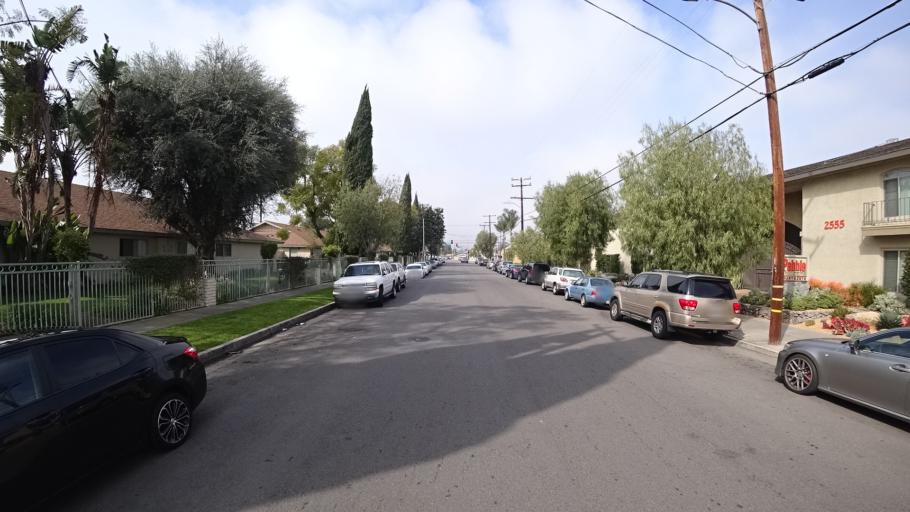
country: US
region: California
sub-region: Orange County
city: Stanton
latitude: 33.8140
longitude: -117.9743
